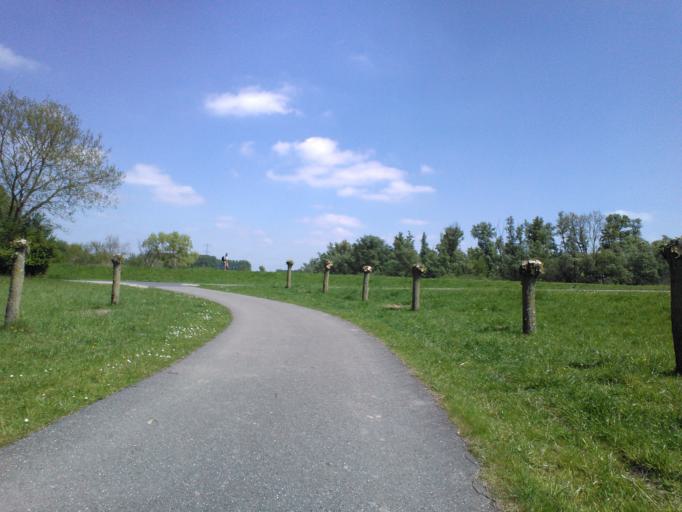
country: NL
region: South Holland
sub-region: Gemeente Sliedrecht
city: Sliedrecht
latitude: 51.8075
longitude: 4.7826
